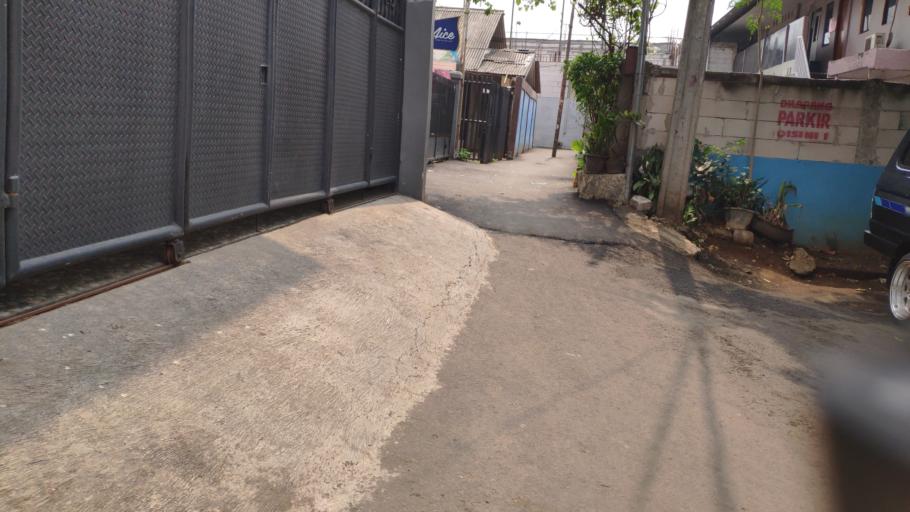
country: ID
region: Jakarta Raya
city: Jakarta
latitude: -6.3058
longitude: 106.8337
